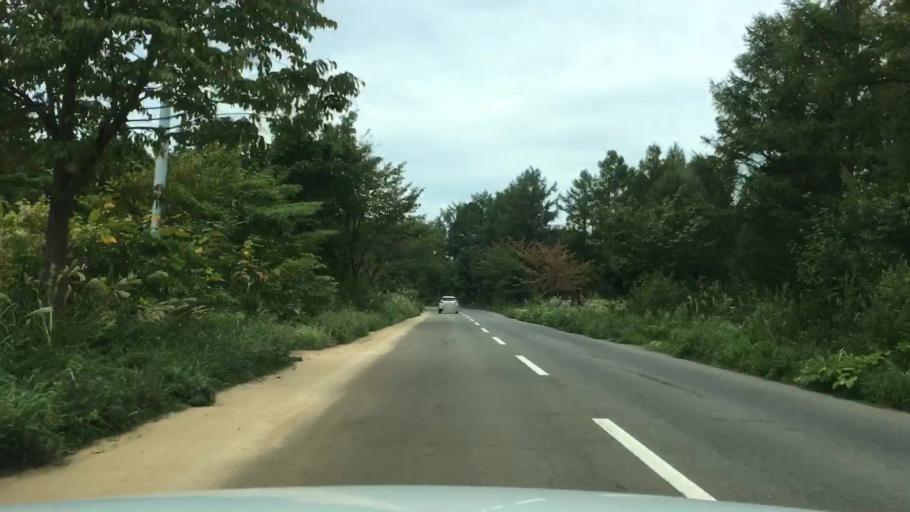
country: JP
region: Aomori
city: Shimokizukuri
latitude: 40.7085
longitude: 140.3389
